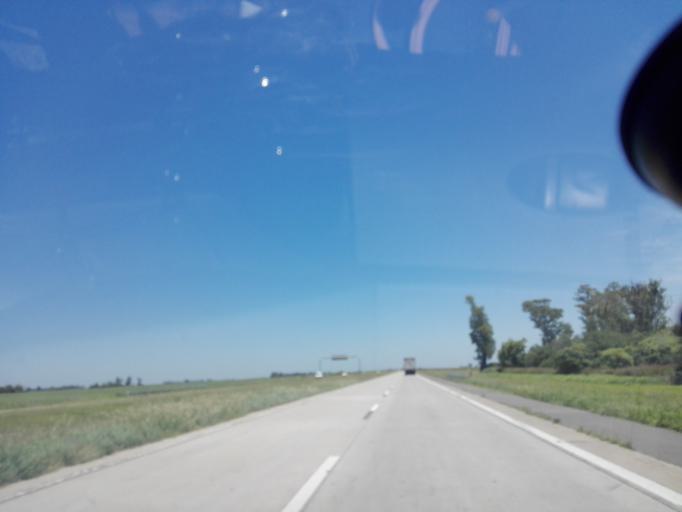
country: AR
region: Cordoba
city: Leones
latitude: -32.6280
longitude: -62.3017
